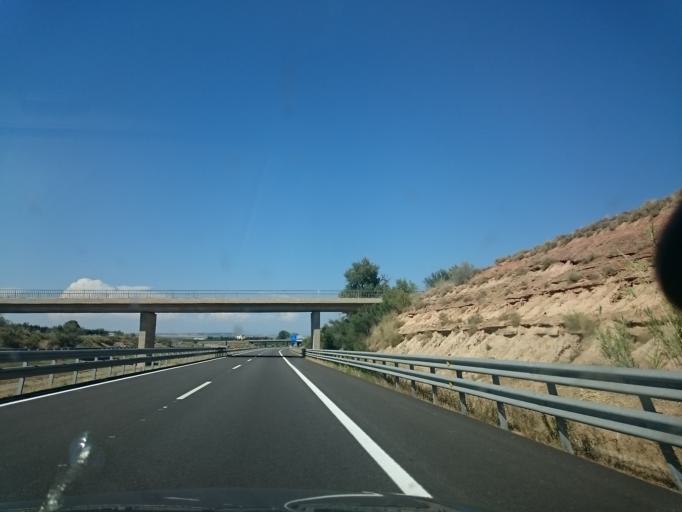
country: ES
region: Catalonia
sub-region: Provincia de Lleida
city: Soses
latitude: 41.5306
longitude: 0.4715
